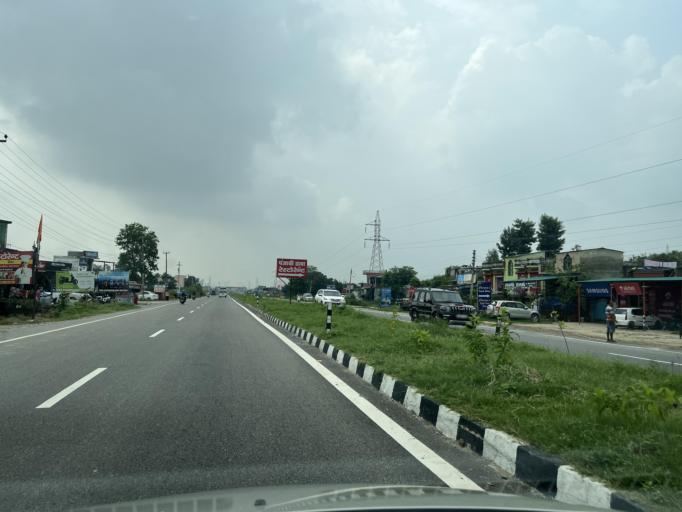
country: IN
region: Uttarakhand
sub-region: Dehradun
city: Raiwala
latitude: 30.0878
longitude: 78.1868
